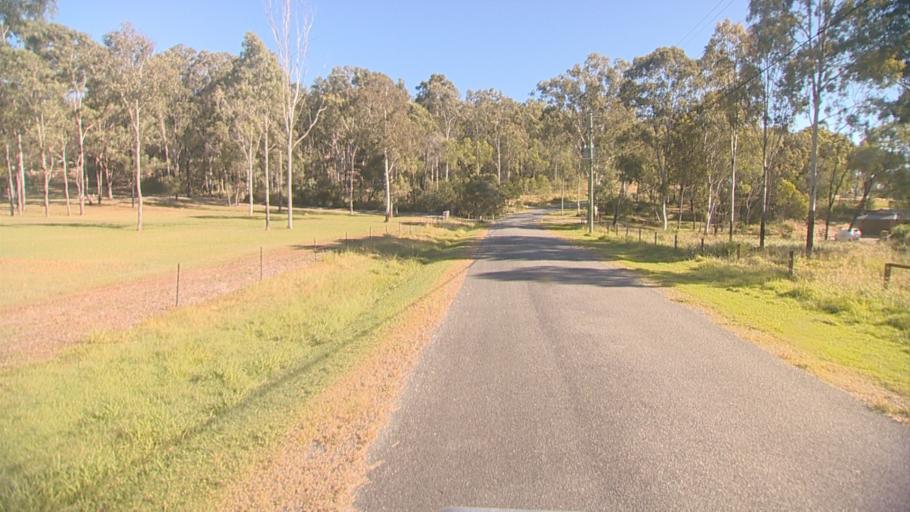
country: AU
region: Queensland
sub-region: Logan
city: Windaroo
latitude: -27.7614
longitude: 153.1483
